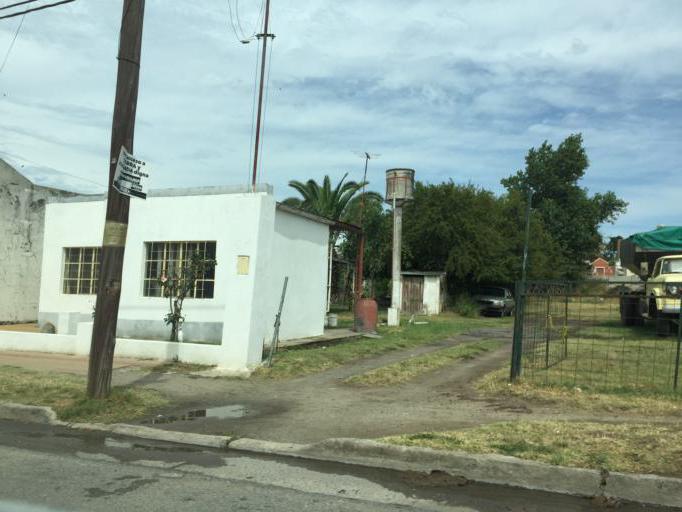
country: AR
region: Buenos Aires
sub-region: Partido de Tandil
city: Tandil
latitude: -37.3206
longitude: -59.1066
